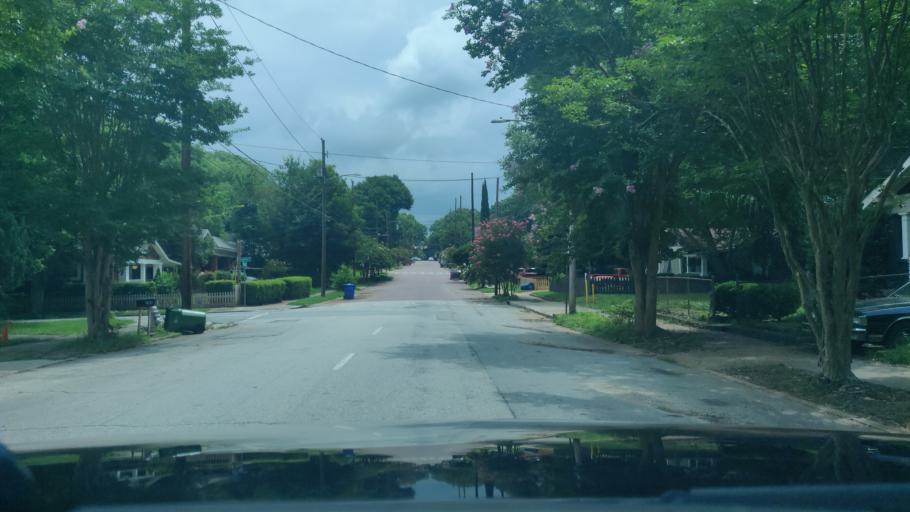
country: US
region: Georgia
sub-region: Fulton County
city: Atlanta
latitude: 33.7303
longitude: -84.3814
